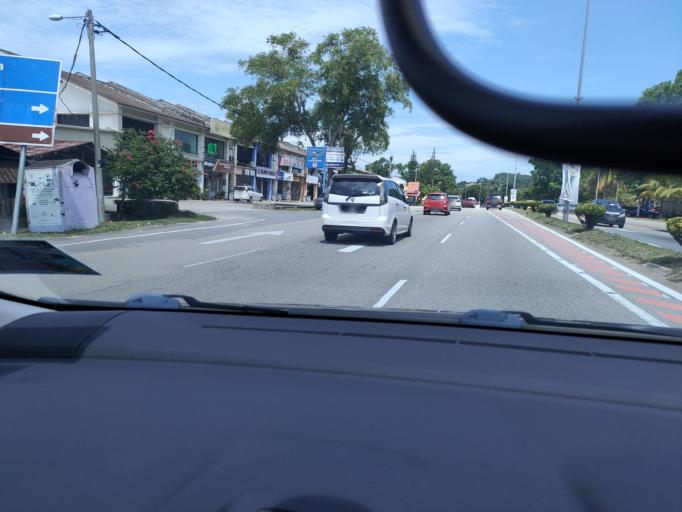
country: MY
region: Melaka
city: Batu Berendam
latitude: 2.2678
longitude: 102.2175
